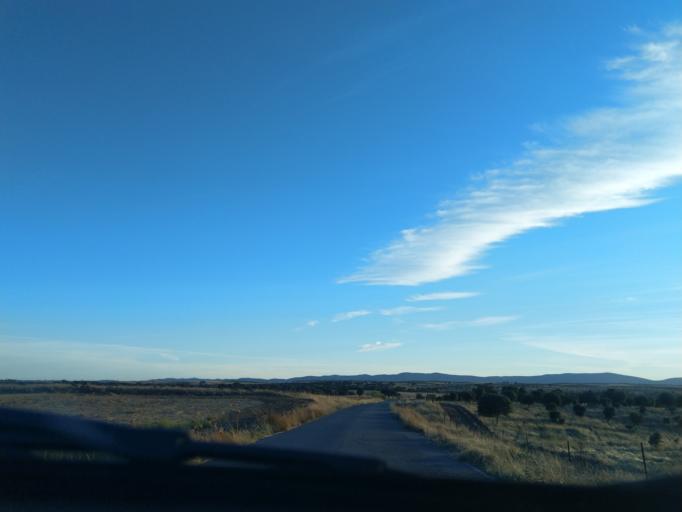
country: ES
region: Extremadura
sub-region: Provincia de Badajoz
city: Ahillones
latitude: 38.2505
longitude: -5.8251
